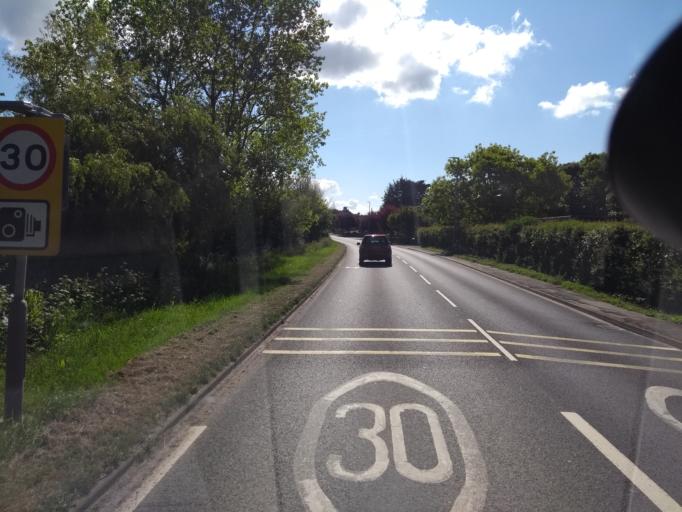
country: GB
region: England
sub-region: Somerset
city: Bridgwater
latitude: 51.1291
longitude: -3.0301
